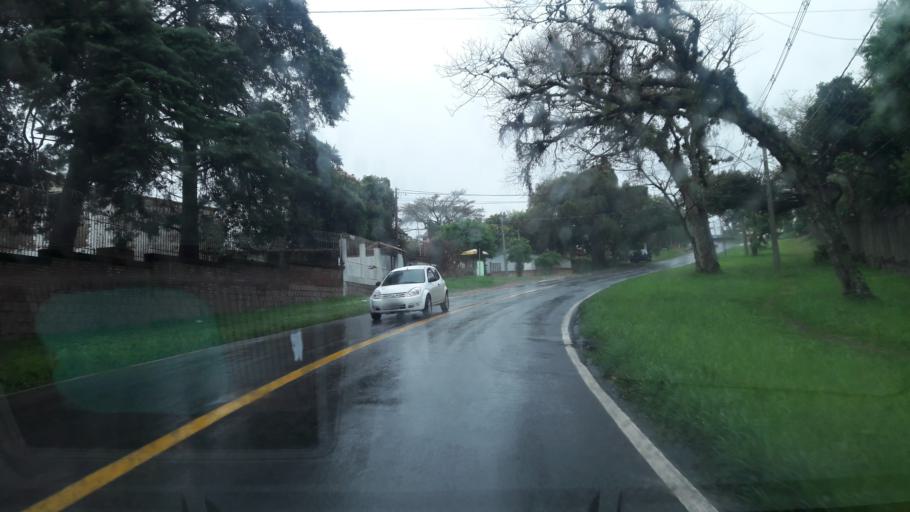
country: BR
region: Rio Grande do Sul
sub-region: Porto Alegre
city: Porto Alegre
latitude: -30.1292
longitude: -51.2235
